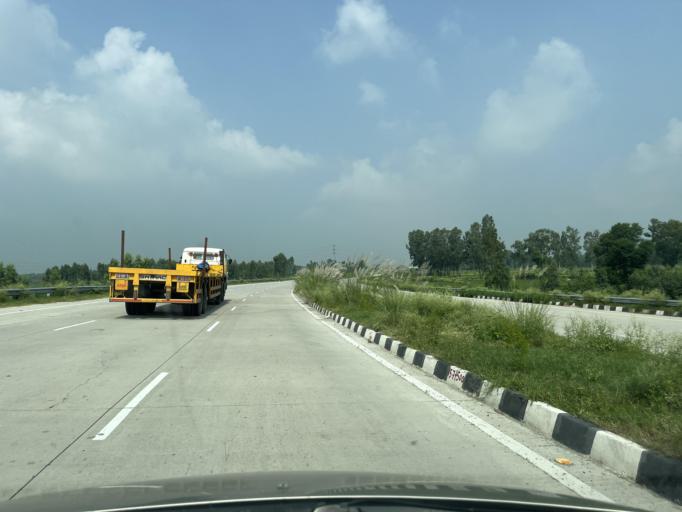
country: IN
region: Uttarakhand
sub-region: Udham Singh Nagar
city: Kashipur
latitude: 29.1636
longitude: 78.9625
